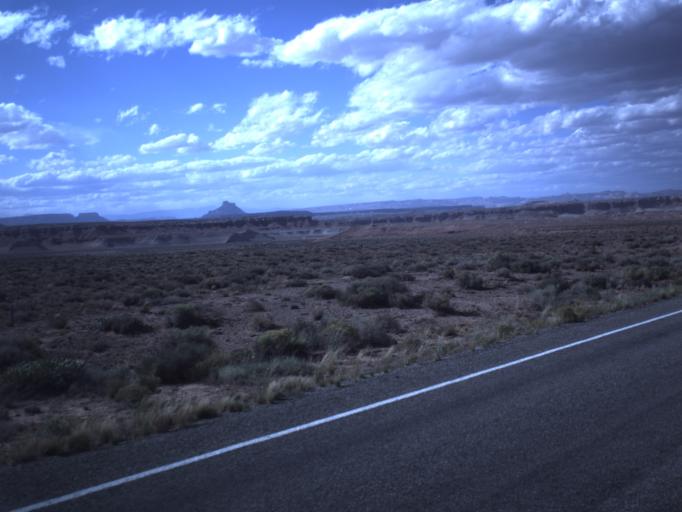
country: US
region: Utah
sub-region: Emery County
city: Ferron
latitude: 38.3456
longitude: -110.6928
